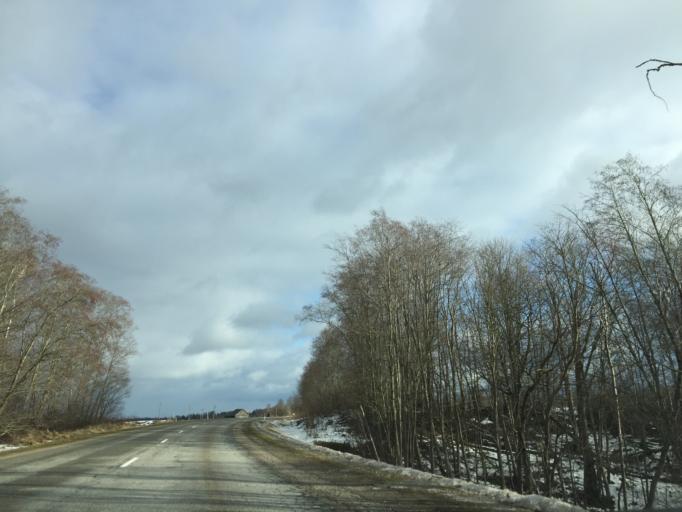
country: LV
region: Aloja
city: Staicele
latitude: 57.8944
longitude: 24.6316
